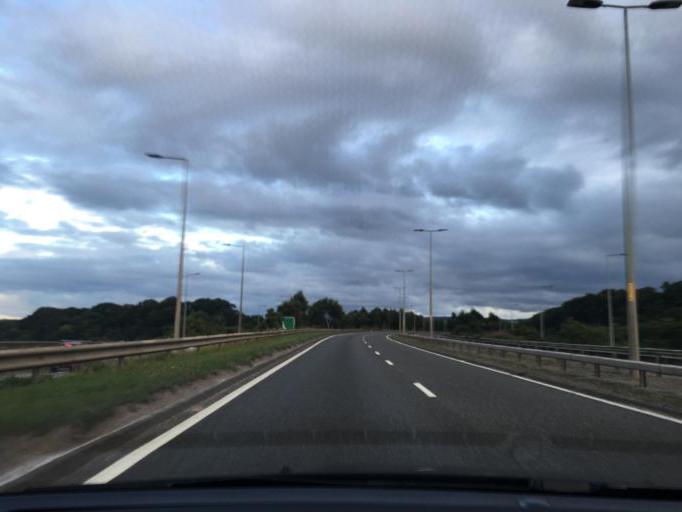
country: GB
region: Scotland
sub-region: Highland
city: Inverness
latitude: 57.4834
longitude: -4.1964
